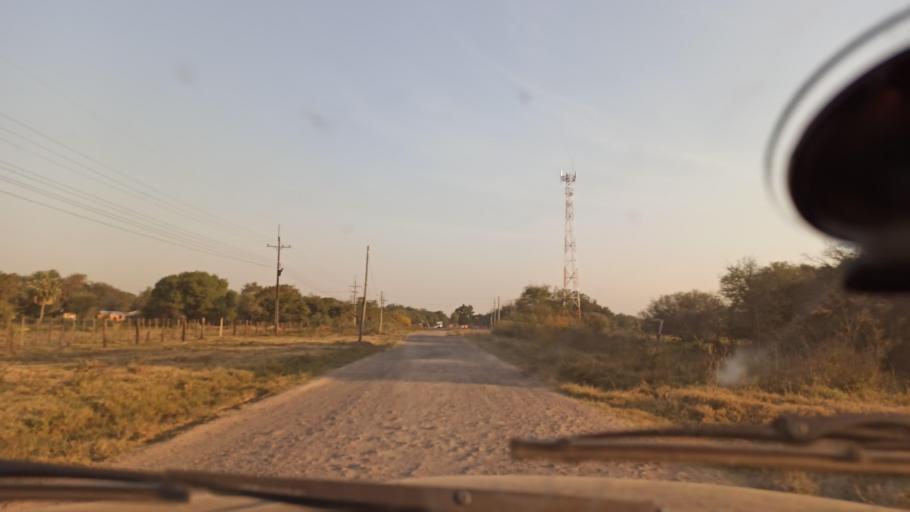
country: PY
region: Presidente Hayes
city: Nanawa
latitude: -25.2312
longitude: -57.6309
